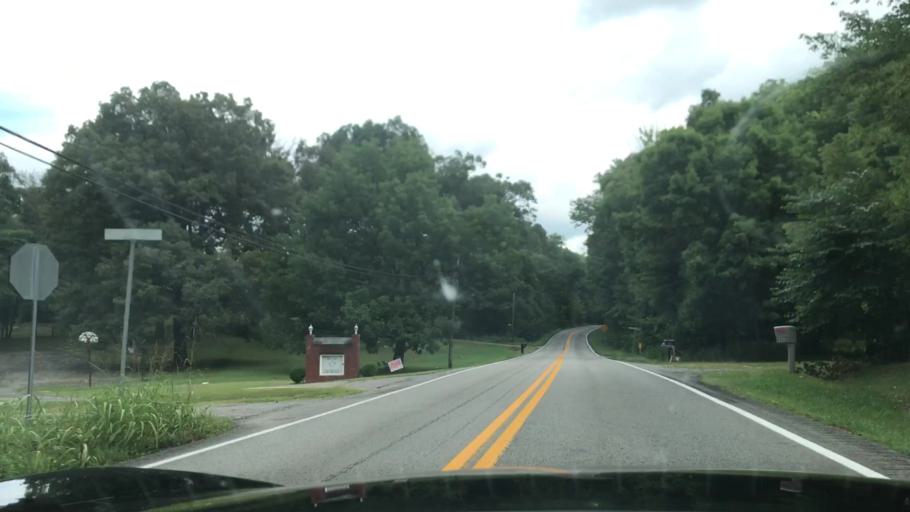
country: US
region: Kentucky
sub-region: Muhlenberg County
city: Central City
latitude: 37.1993
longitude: -87.0301
